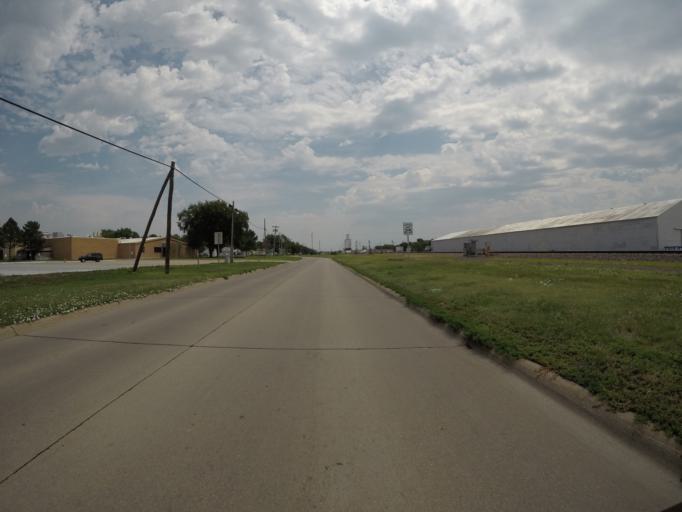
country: US
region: Nebraska
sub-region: Buffalo County
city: Kearney
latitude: 40.6939
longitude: -99.0963
